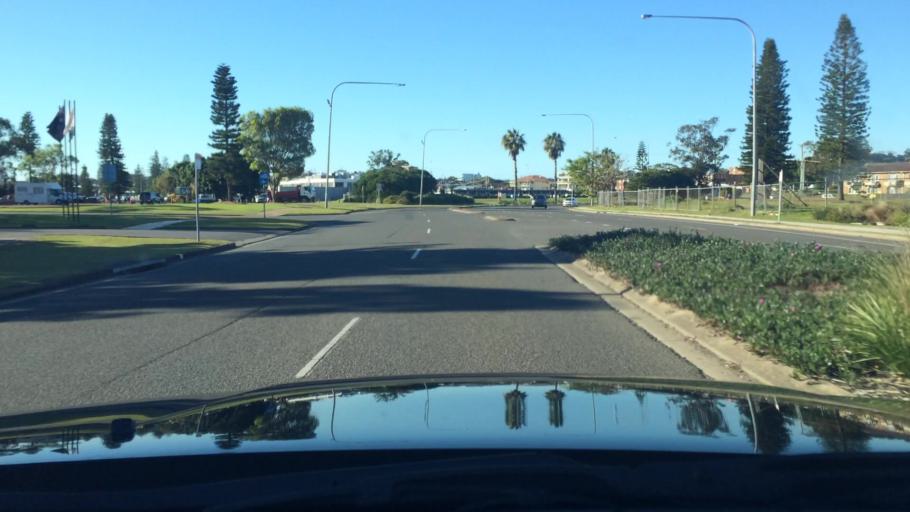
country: AU
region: New South Wales
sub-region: Port Macquarie-Hastings
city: Port Macquarie
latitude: -31.4288
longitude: 152.8986
